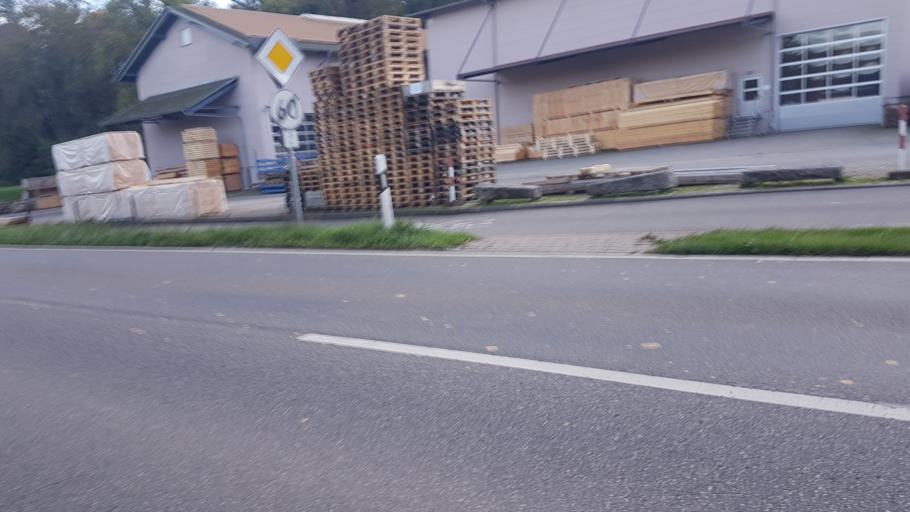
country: DE
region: Baden-Wuerttemberg
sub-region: Karlsruhe Region
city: Neckarzimmern
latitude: 49.3243
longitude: 9.1069
